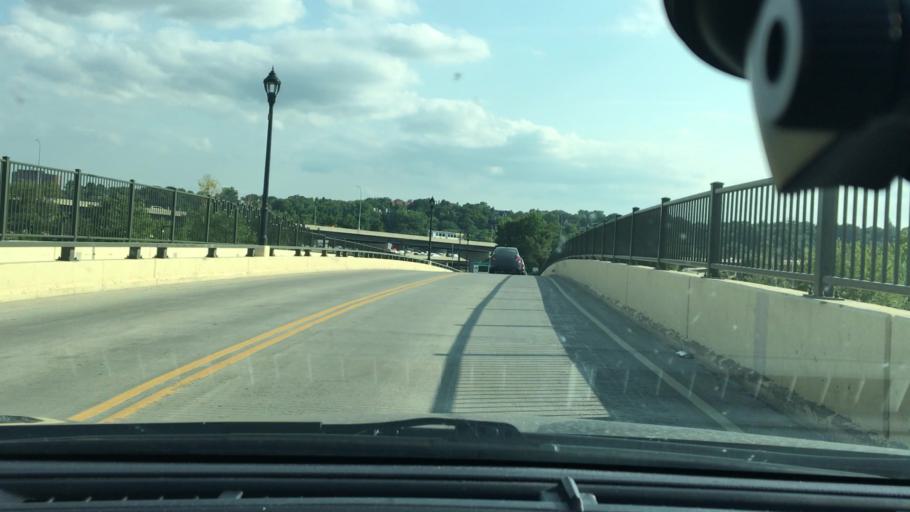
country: US
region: Minnesota
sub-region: Hennepin County
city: Minneapolis
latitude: 44.9752
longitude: -93.2952
